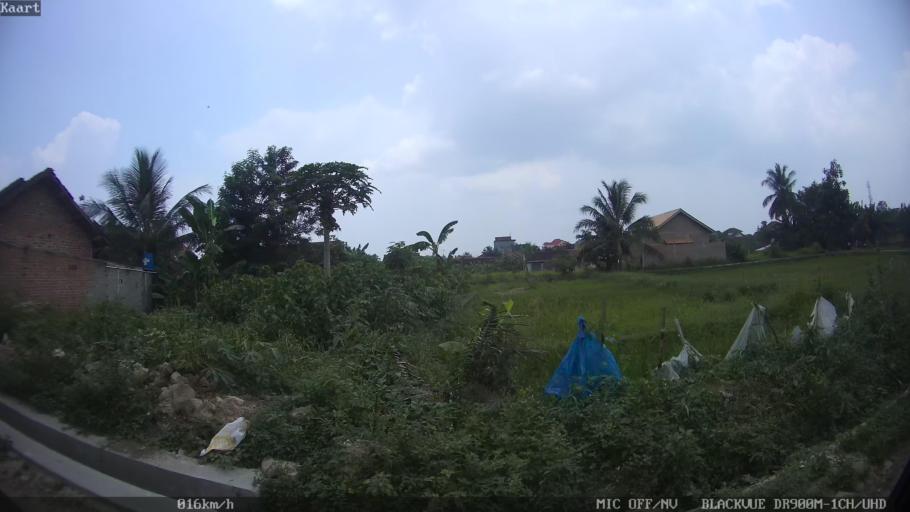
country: ID
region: Lampung
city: Pringsewu
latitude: -5.3465
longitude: 104.9775
